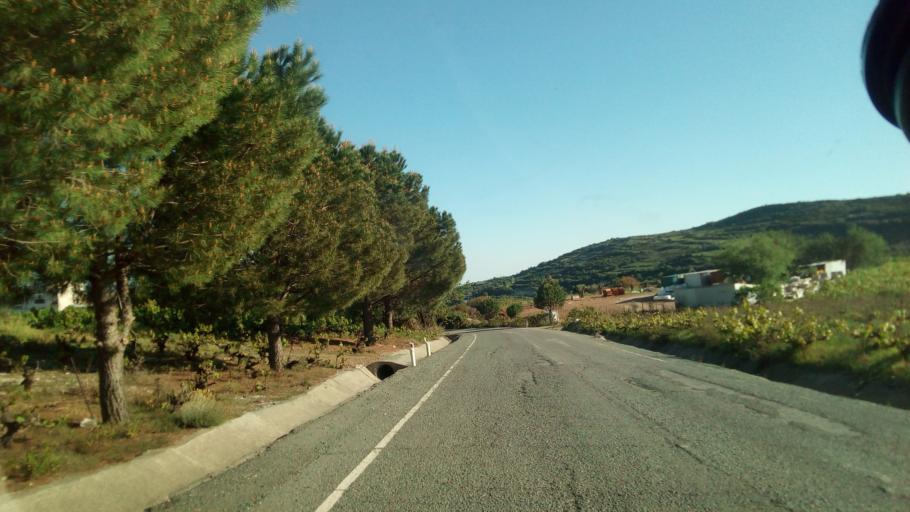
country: CY
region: Limassol
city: Pachna
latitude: 34.8558
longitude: 32.8060
